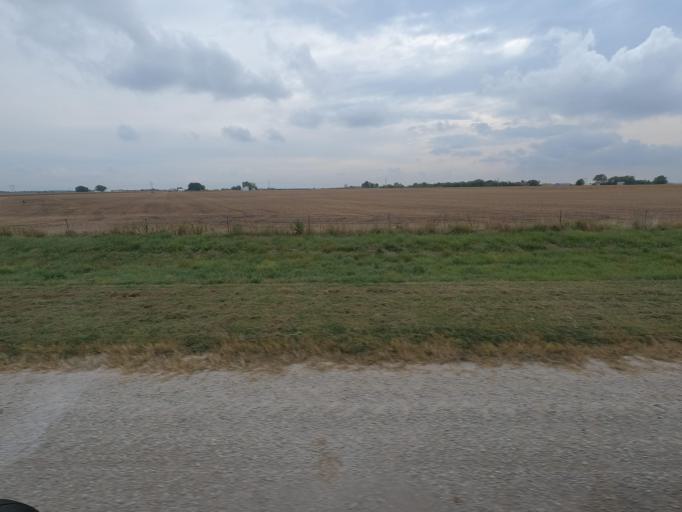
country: US
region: Iowa
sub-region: Wapello County
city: Ottumwa
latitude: 41.0952
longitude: -92.4511
